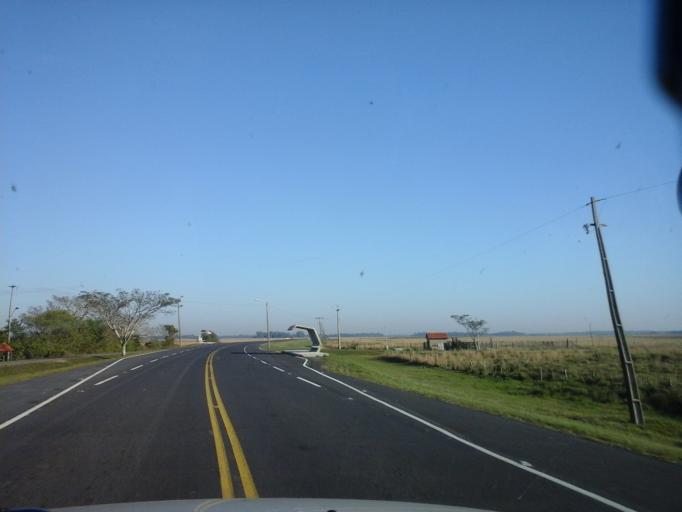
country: PY
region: Neembucu
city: Pilar
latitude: -26.8710
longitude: -57.9259
